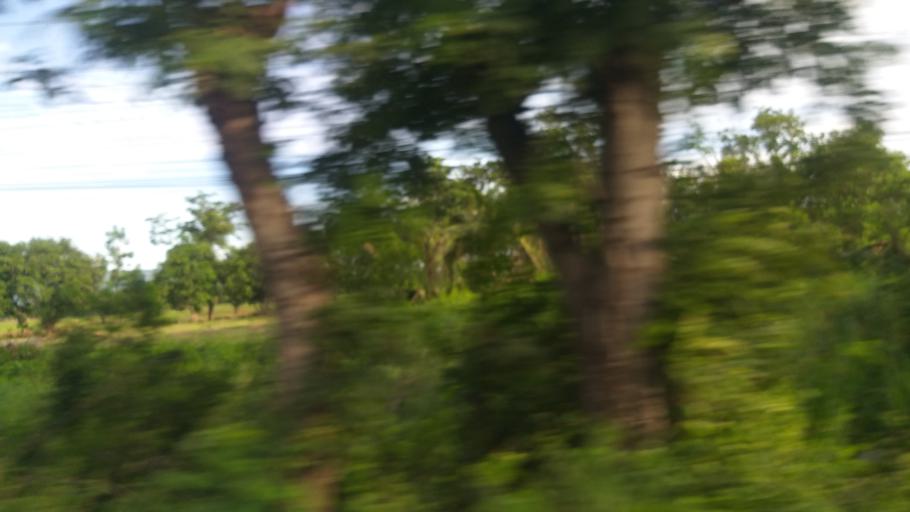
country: TH
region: Chaiyaphum
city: Ban Thaen
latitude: 16.3888
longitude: 102.3250
